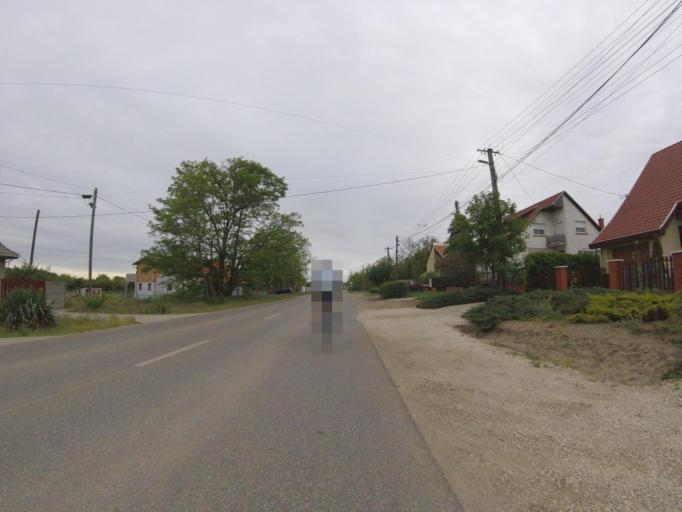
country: HU
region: Pest
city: Inarcs
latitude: 47.2494
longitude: 19.3375
